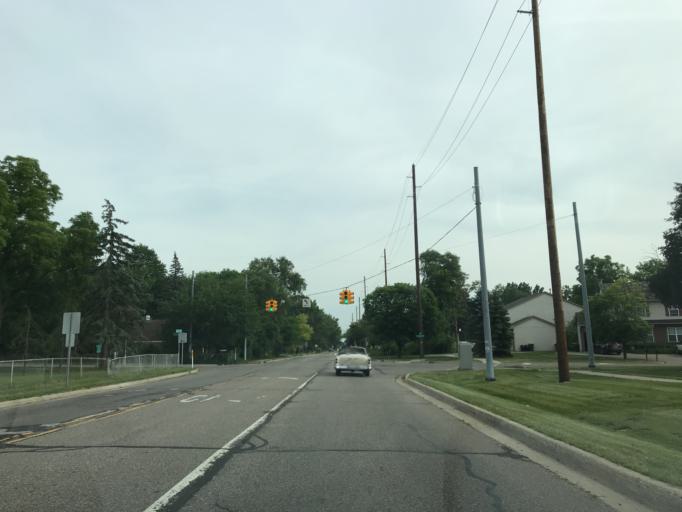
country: US
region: Michigan
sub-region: Oakland County
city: Farmington
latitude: 42.4504
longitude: -83.3173
